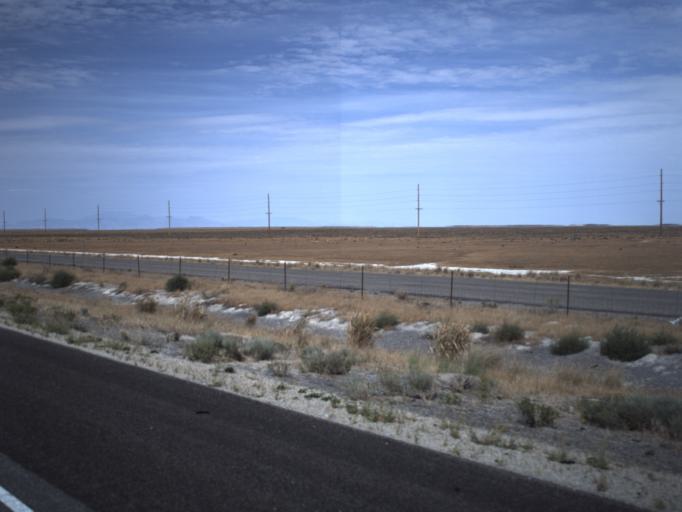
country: US
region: Utah
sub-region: Tooele County
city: Grantsville
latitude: 40.7262
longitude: -113.1640
